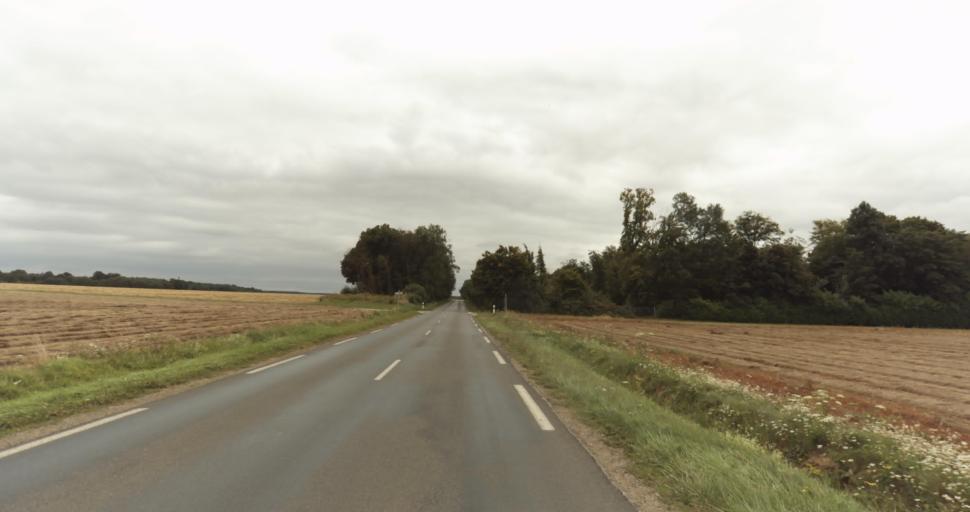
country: FR
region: Haute-Normandie
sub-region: Departement de l'Eure
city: Gravigny
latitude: 49.0204
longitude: 1.2426
